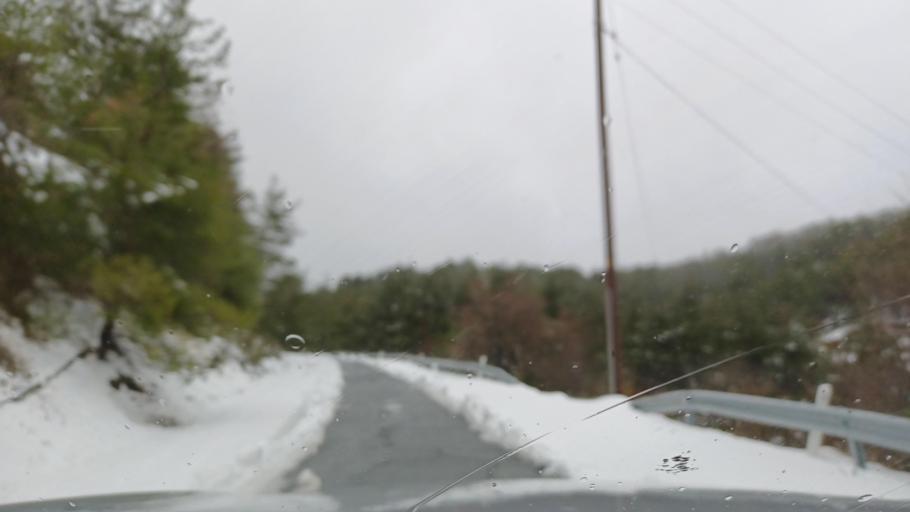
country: CY
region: Limassol
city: Pelendri
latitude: 34.9104
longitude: 32.9563
